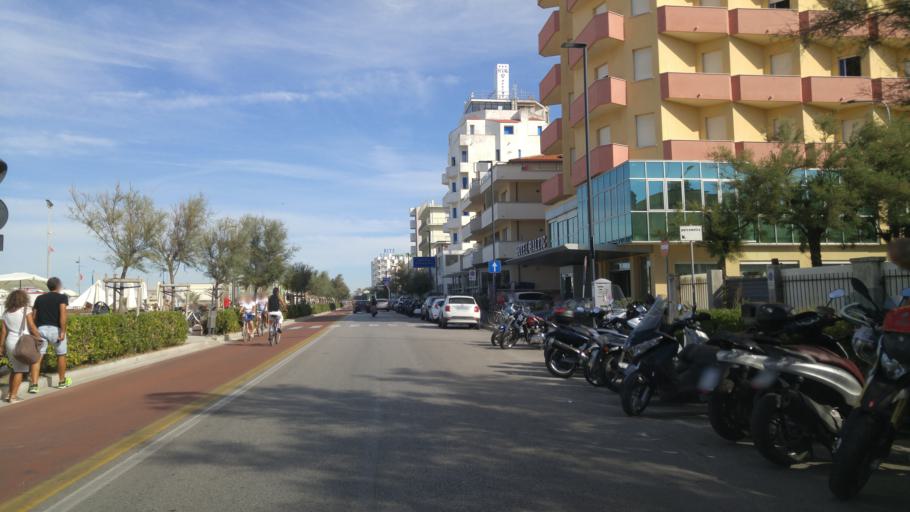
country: IT
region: The Marches
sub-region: Provincia di Ancona
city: Senigallia
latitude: 43.7094
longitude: 13.2334
